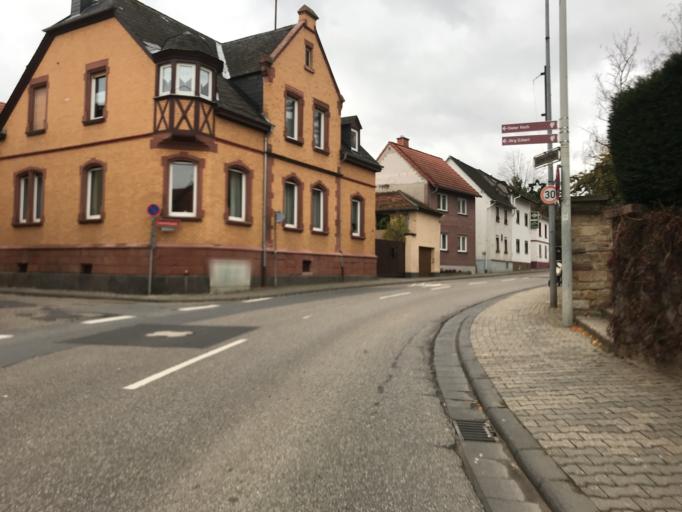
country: DE
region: Rheinland-Pfalz
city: Harxheim
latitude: 49.9131
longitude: 8.2439
